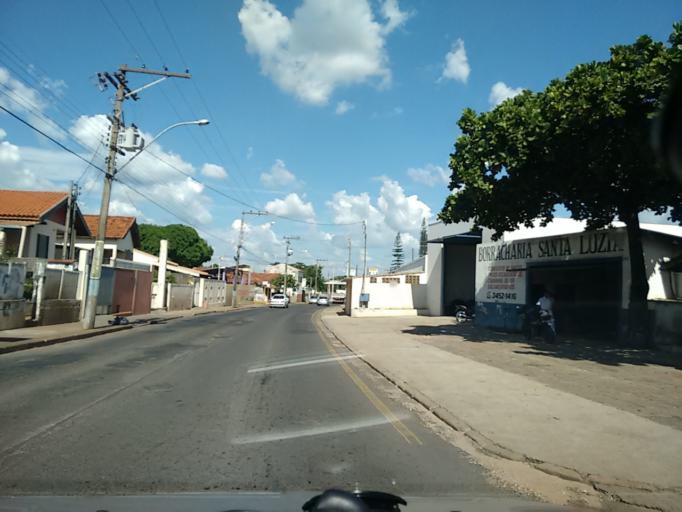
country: BR
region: Sao Paulo
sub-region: Pompeia
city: Pompeia
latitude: -22.1069
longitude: -50.1658
